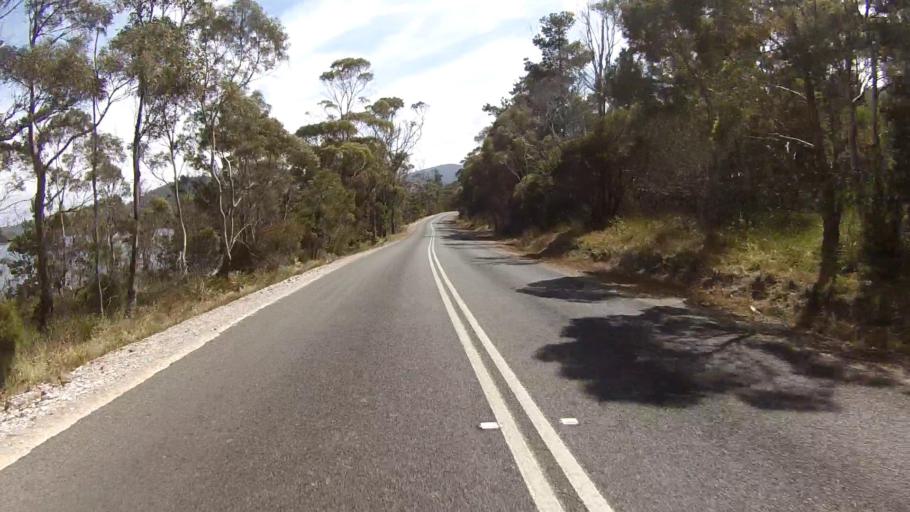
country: AU
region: Tasmania
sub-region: Huon Valley
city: Cygnet
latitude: -43.2651
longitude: 147.1427
